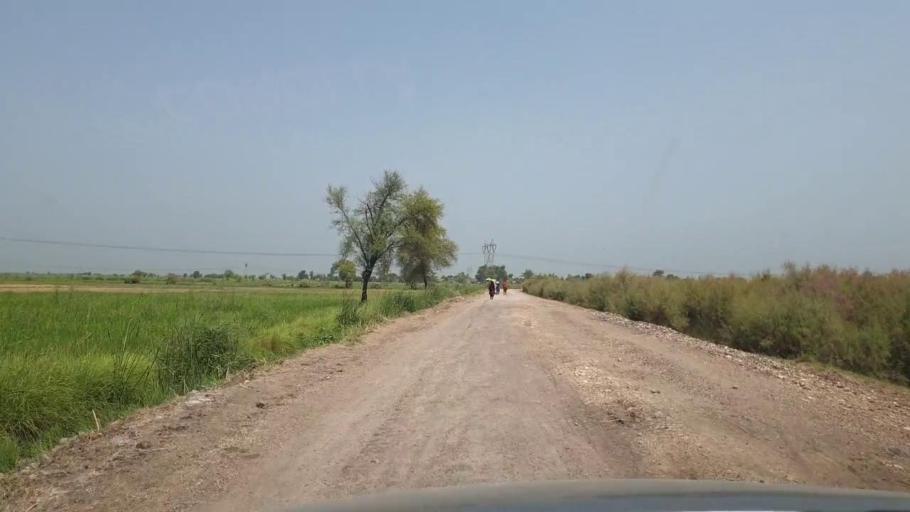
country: PK
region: Sindh
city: Madeji
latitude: 27.8018
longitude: 68.5206
